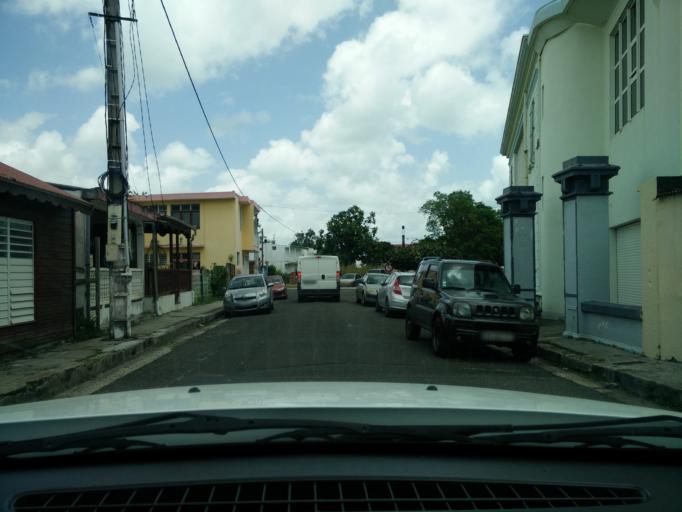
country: GP
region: Guadeloupe
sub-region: Guadeloupe
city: Port-Louis
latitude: 16.4171
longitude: -61.5323
